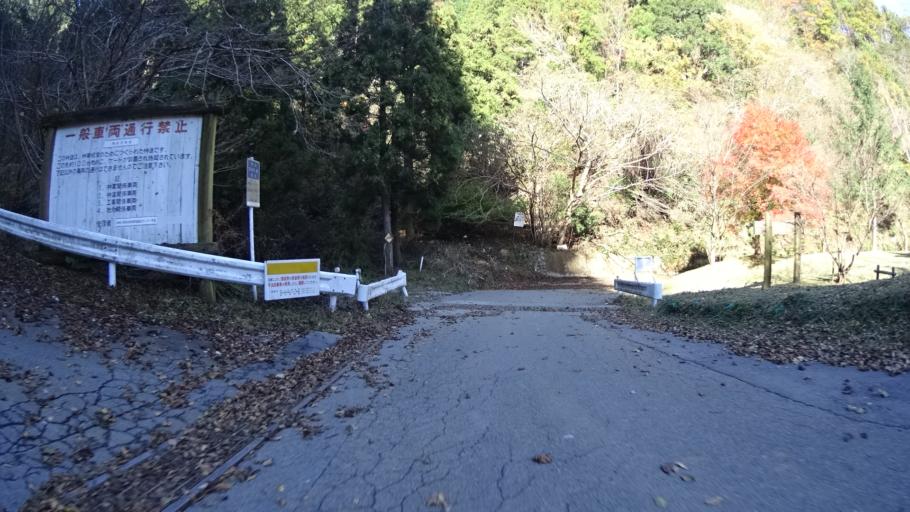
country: JP
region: Kanagawa
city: Atsugi
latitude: 35.5104
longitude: 139.2682
